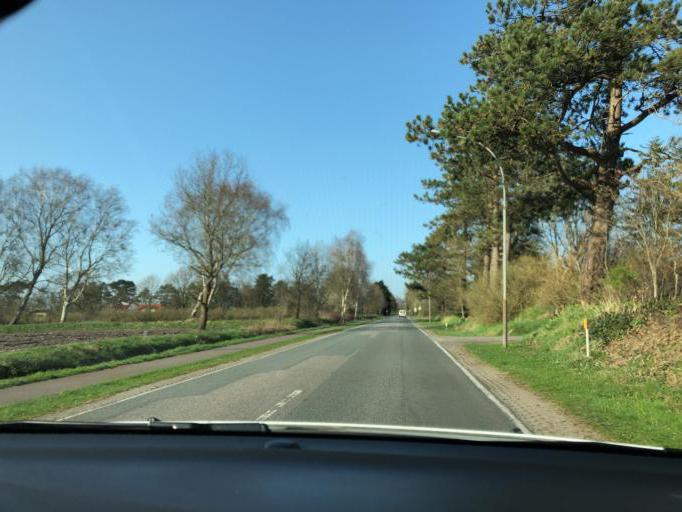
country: DE
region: Schleswig-Holstein
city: Bargum
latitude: 54.6867
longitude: 8.9624
